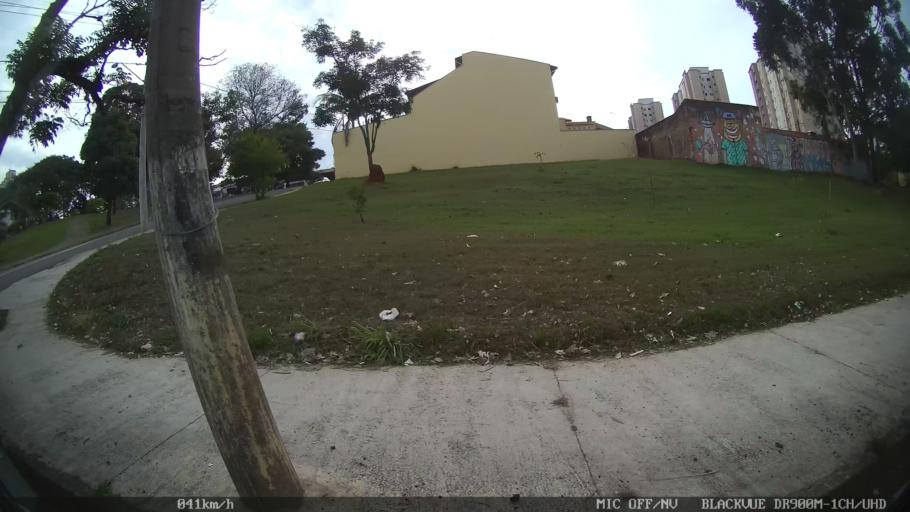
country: BR
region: Sao Paulo
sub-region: Piracicaba
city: Piracicaba
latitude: -22.7457
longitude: -47.6326
